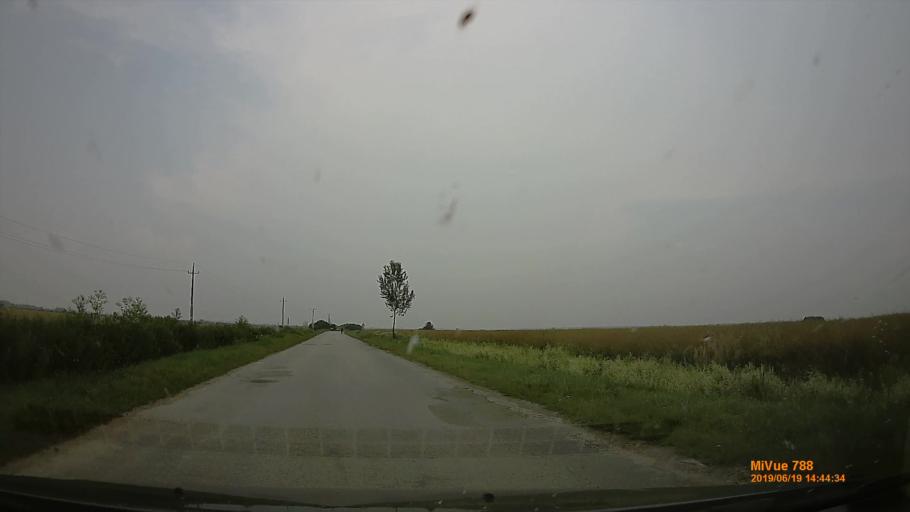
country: HU
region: Baranya
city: Szigetvar
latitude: 46.0264
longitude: 17.8286
